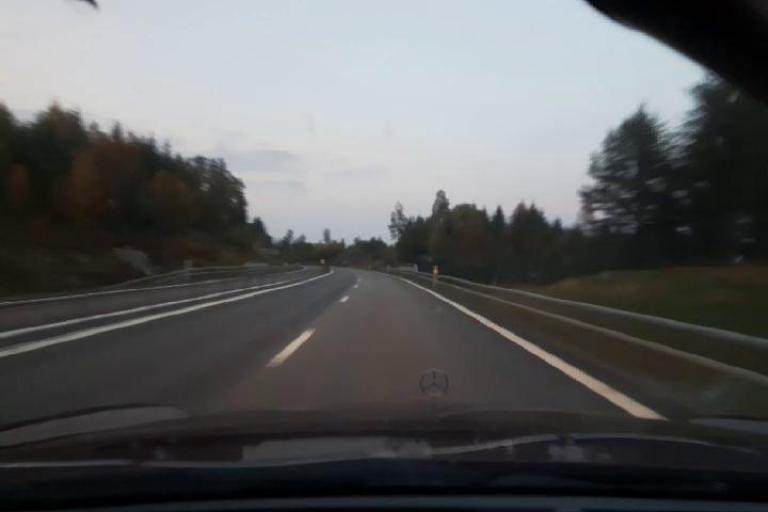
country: SE
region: Vaesternorrland
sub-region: Kramfors Kommun
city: Nordingra
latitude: 62.8815
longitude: 18.0831
